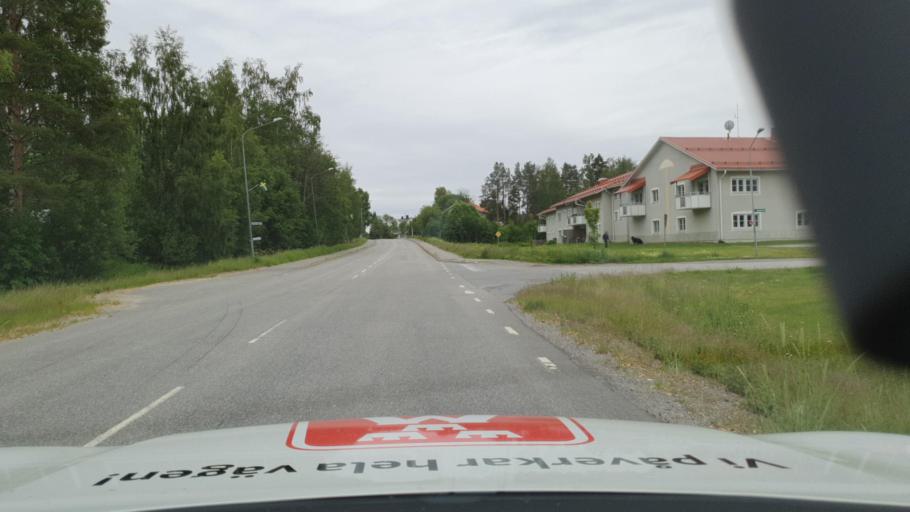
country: SE
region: Vaesterbotten
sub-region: Nordmalings Kommun
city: Nordmaling
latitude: 63.5437
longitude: 19.4386
